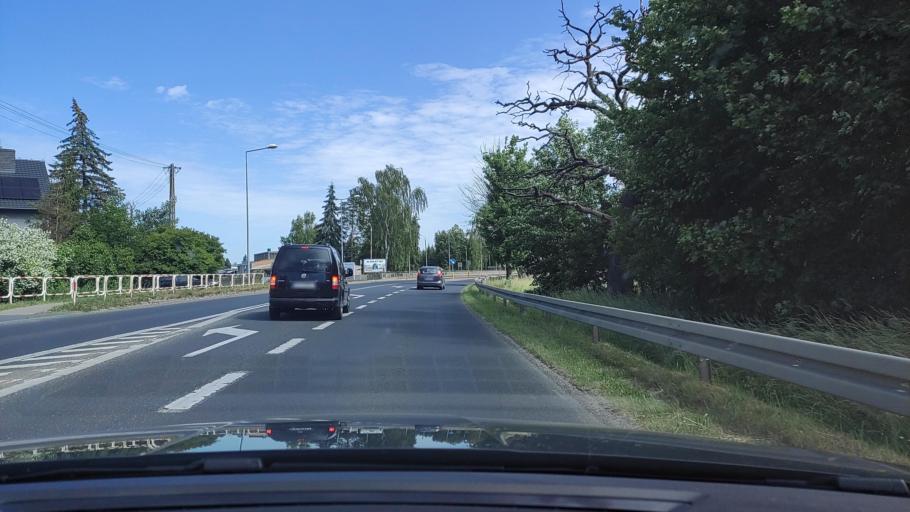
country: PL
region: Greater Poland Voivodeship
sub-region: Powiat poznanski
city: Murowana Goslina
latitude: 52.5308
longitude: 16.9782
